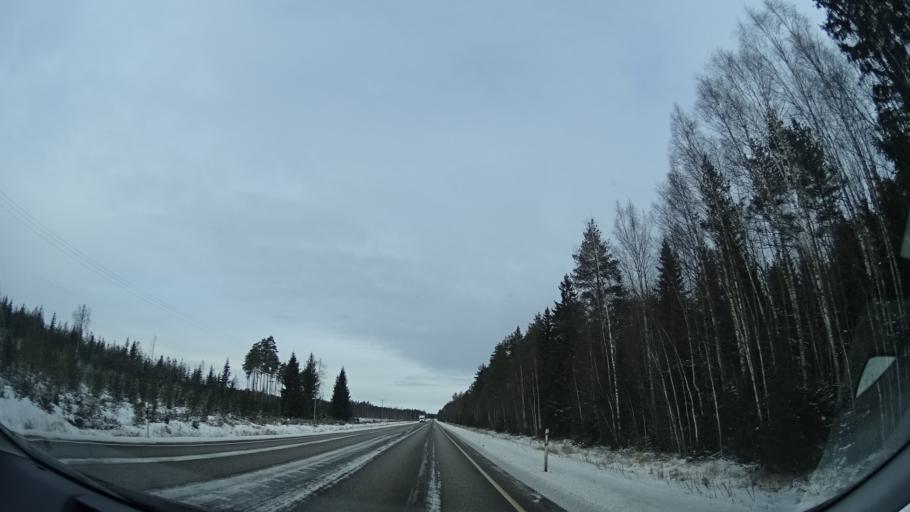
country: FI
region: Uusimaa
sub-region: Helsinki
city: Kaerkoelae
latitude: 60.6735
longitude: 23.8212
